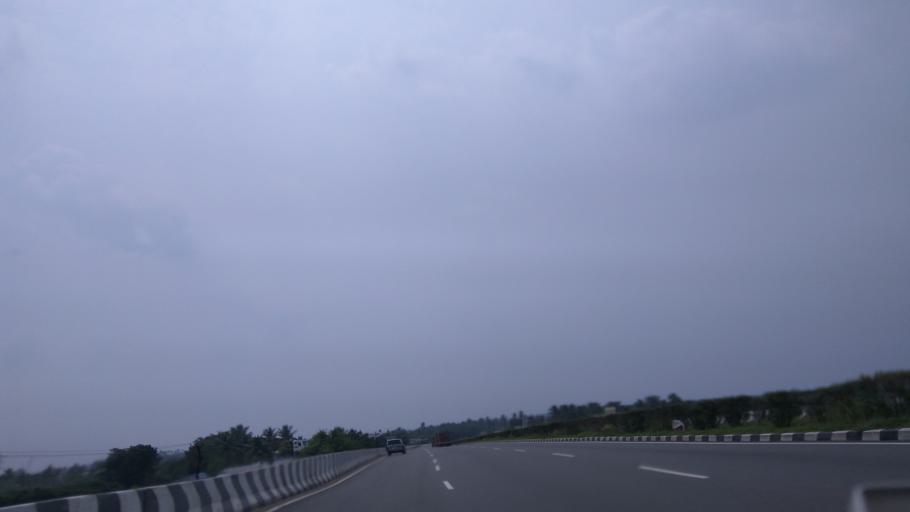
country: IN
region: Tamil Nadu
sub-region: Krishnagiri
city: Kaverippattanam
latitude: 12.3031
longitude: 78.2081
